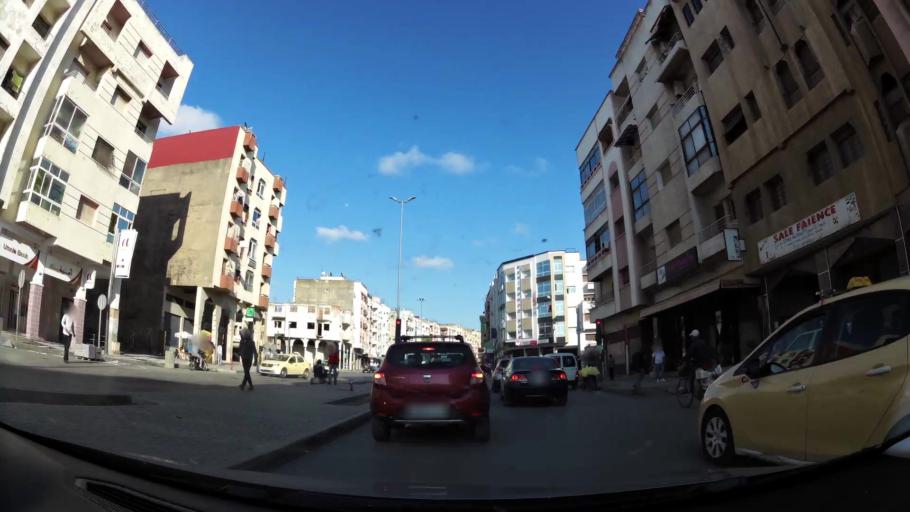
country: MA
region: Rabat-Sale-Zemmour-Zaer
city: Sale
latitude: 34.0549
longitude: -6.7944
